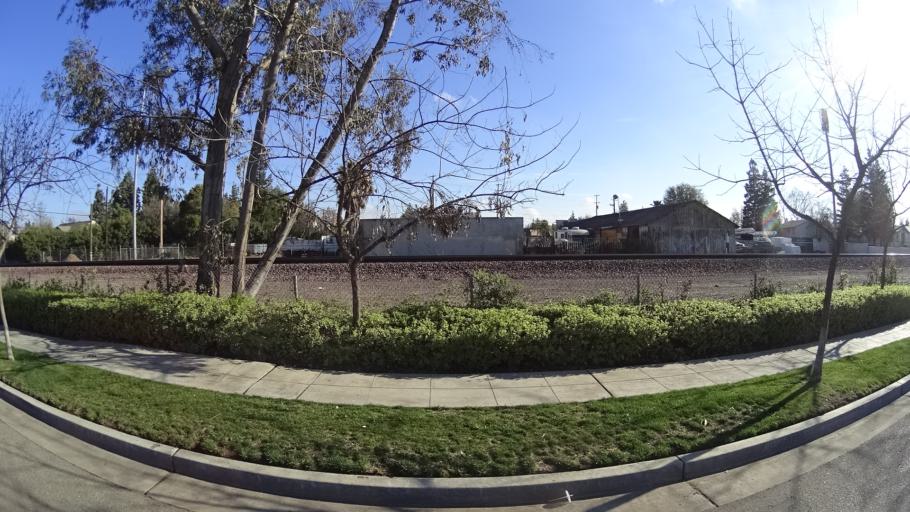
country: US
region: California
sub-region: Fresno County
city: West Park
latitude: 36.8221
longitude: -119.8629
